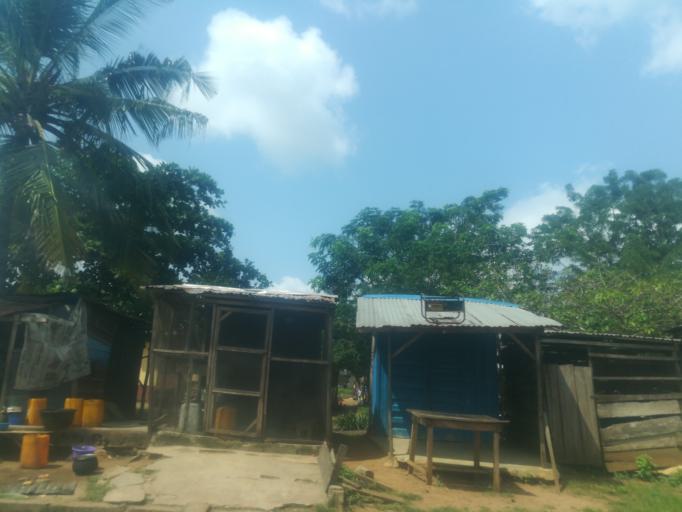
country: NG
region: Oyo
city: Moniya
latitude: 7.5359
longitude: 3.9118
